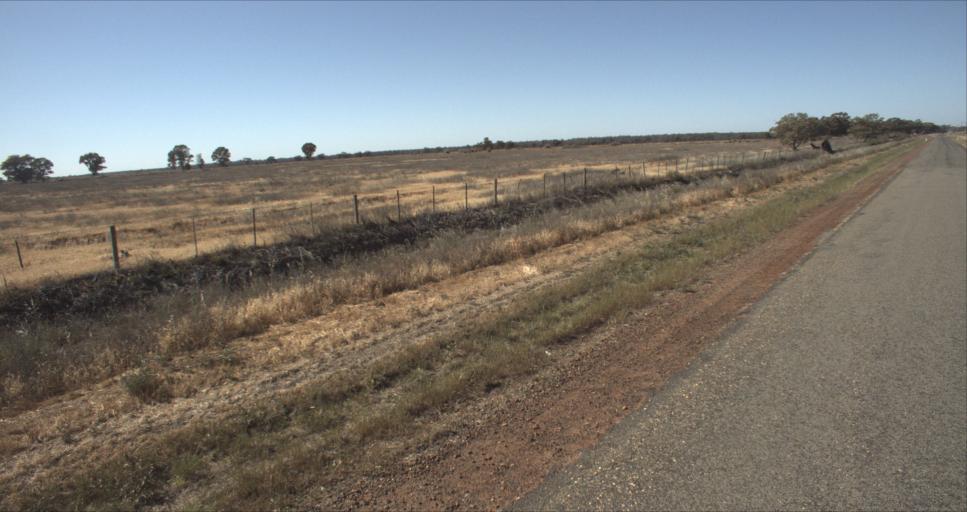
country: AU
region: New South Wales
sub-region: Leeton
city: Leeton
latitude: -34.5845
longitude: 146.2609
